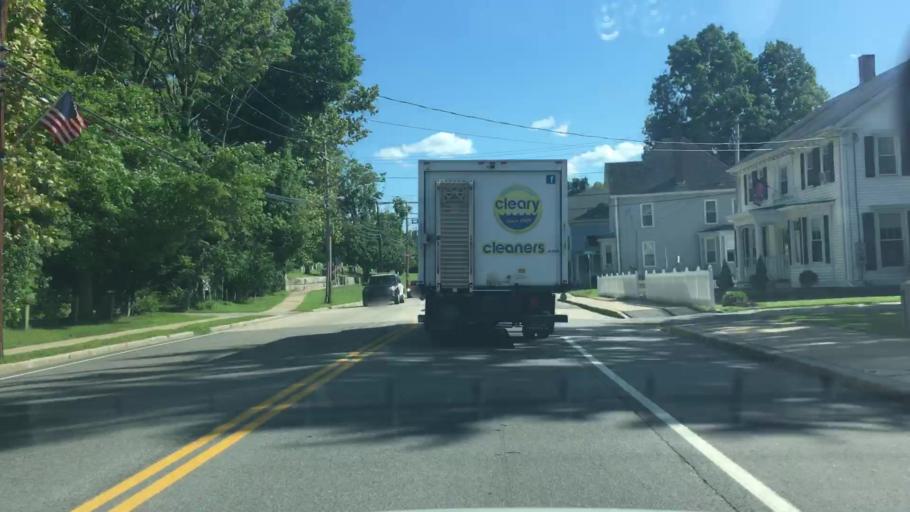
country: US
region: New Hampshire
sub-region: Strafford County
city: Dover
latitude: 43.1874
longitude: -70.8740
